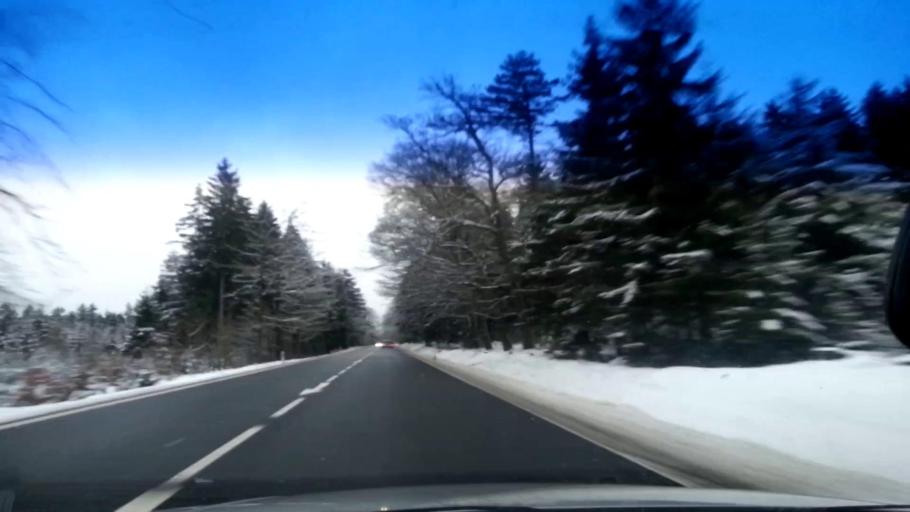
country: CZ
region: Karlovarsky
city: As
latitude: 50.1917
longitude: 12.2248
